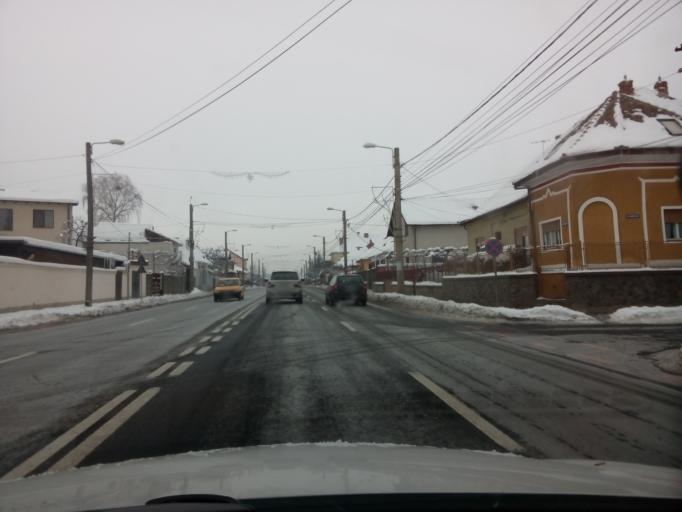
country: RO
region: Sibiu
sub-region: Municipiul Sibiu
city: Sibiu
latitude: 45.7906
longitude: 24.1640
